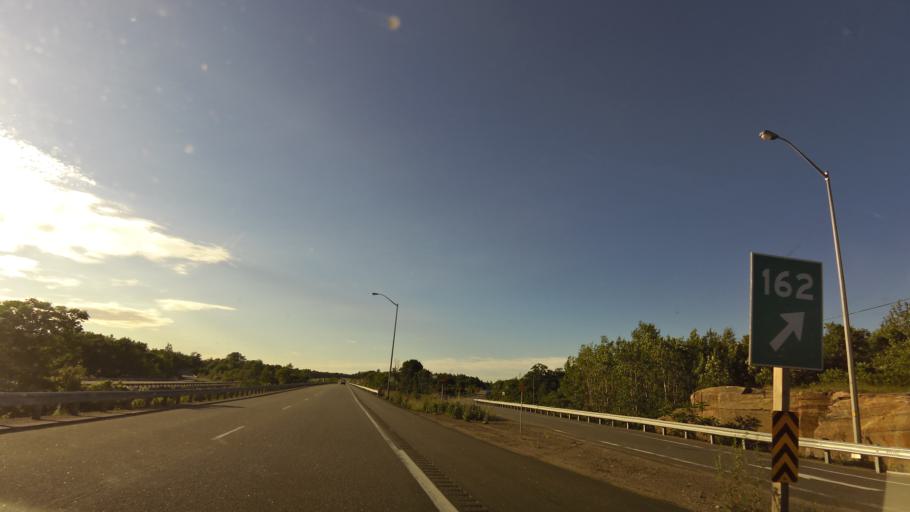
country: CA
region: Ontario
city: Midland
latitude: 44.8554
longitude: -79.7393
